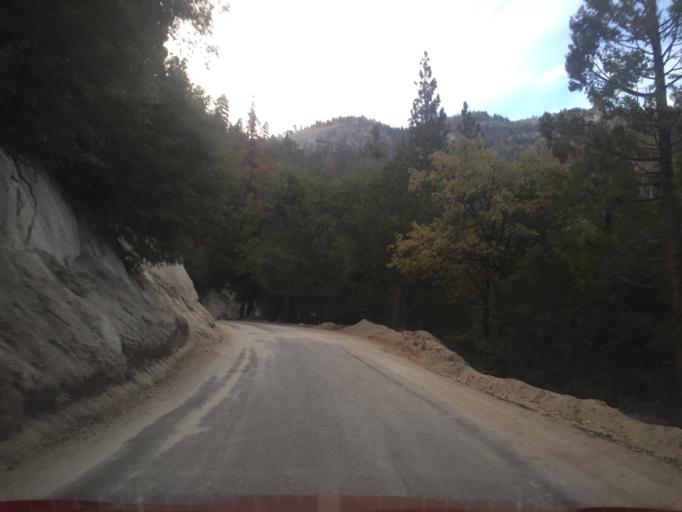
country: US
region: California
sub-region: Tulare County
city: Three Rivers
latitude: 36.4507
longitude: -118.7039
